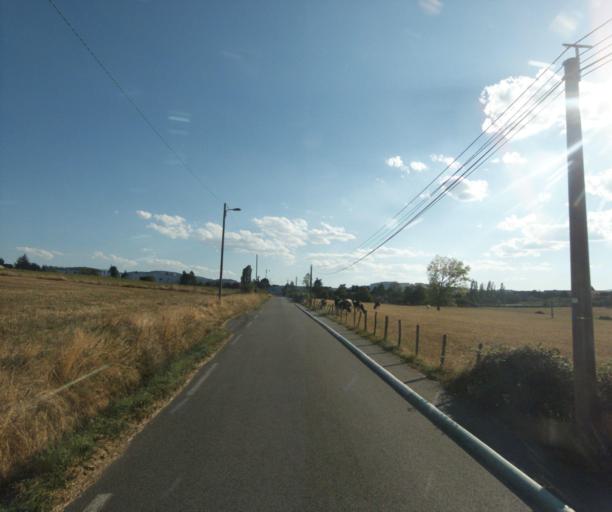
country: FR
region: Rhone-Alpes
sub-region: Departement du Rhone
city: Lentilly
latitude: 45.8285
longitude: 4.6747
